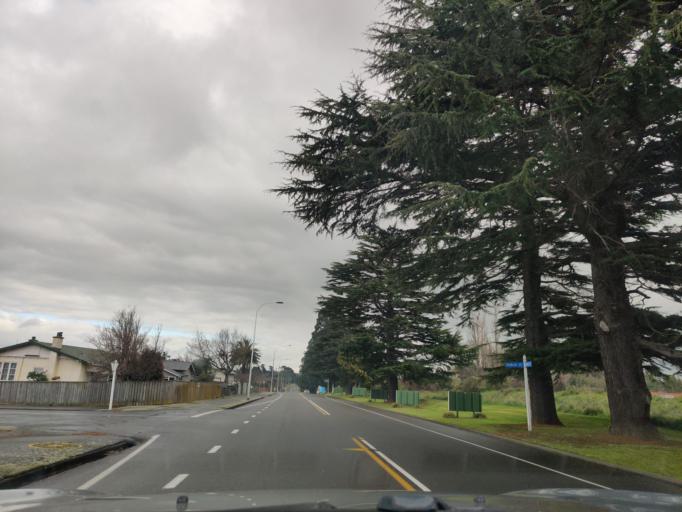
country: NZ
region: Manawatu-Wanganui
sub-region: Palmerston North City
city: Palmerston North
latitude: -40.2115
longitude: 176.0925
